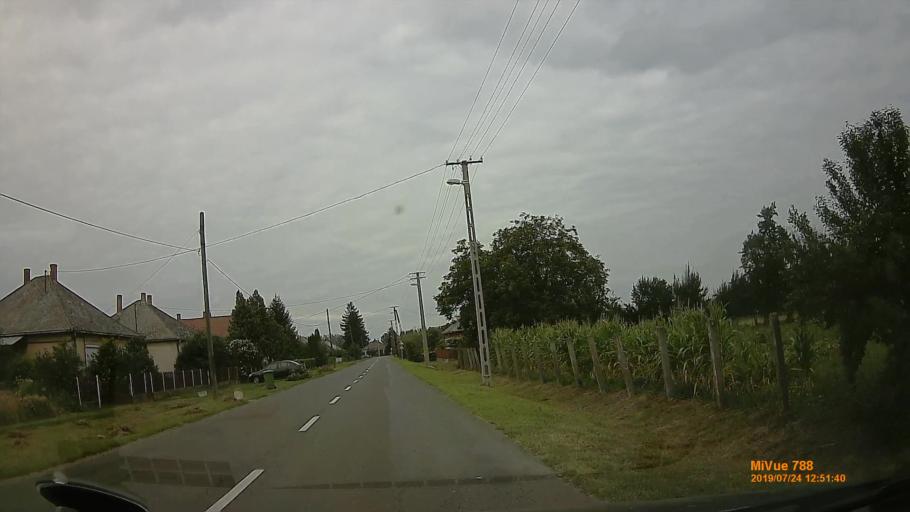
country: HU
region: Szabolcs-Szatmar-Bereg
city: Aranyosapati
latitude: 48.1938
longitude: 22.2980
